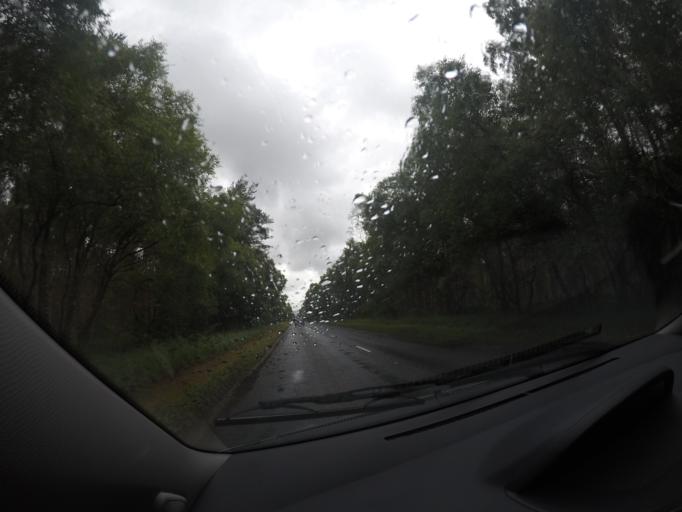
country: GB
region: Scotland
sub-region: Angus
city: Brechin
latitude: 56.7957
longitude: -2.6493
